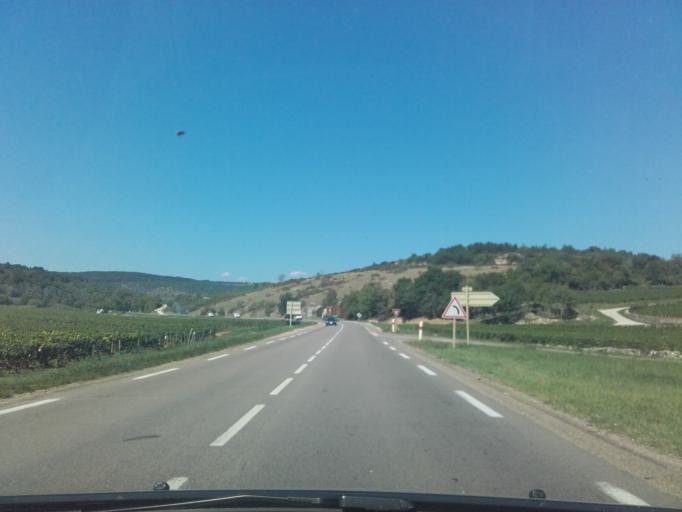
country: FR
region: Bourgogne
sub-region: Departement de la Cote-d'Or
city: Corpeau
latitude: 46.9410
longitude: 4.7351
